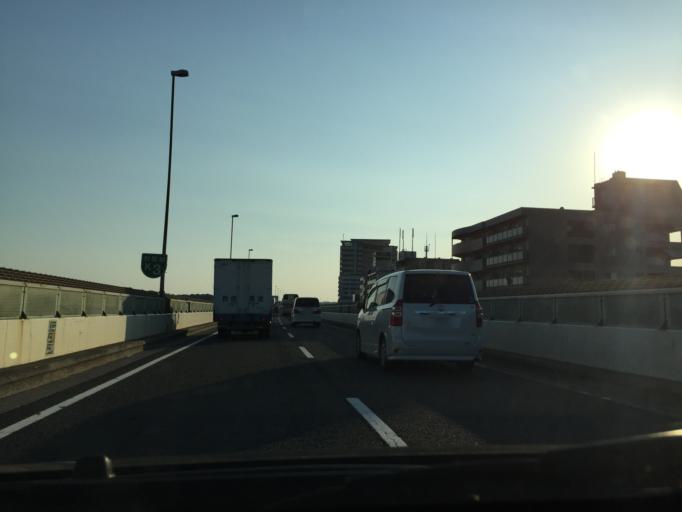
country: JP
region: Kanagawa
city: Yokohama
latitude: 35.4351
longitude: 139.6310
